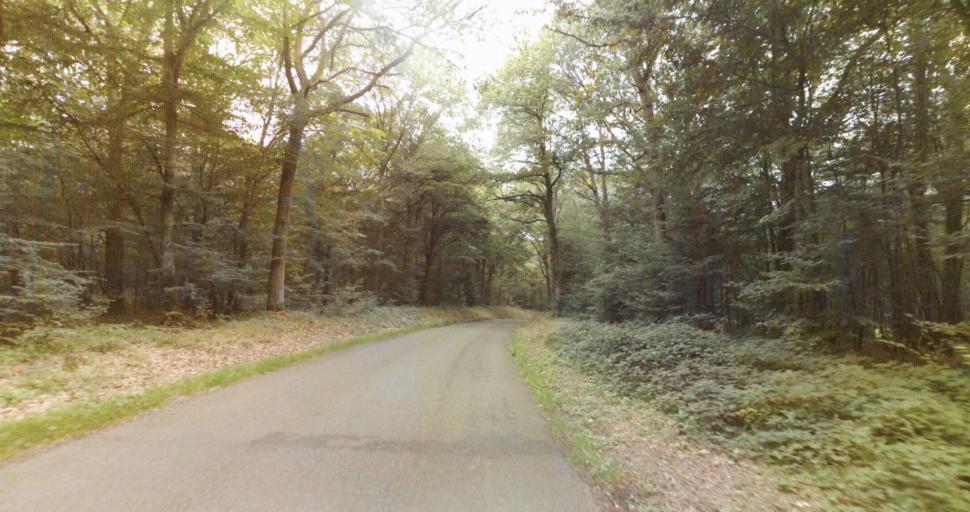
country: FR
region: Haute-Normandie
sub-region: Departement de l'Eure
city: Marcilly-sur-Eure
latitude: 48.8744
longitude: 1.3210
